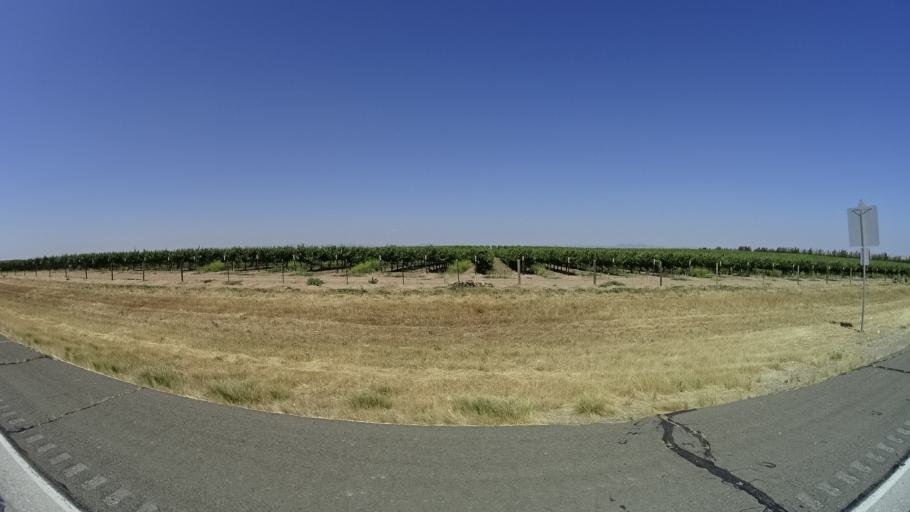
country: US
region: California
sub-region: Monterey County
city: King City
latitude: 36.0612
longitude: -120.9791
